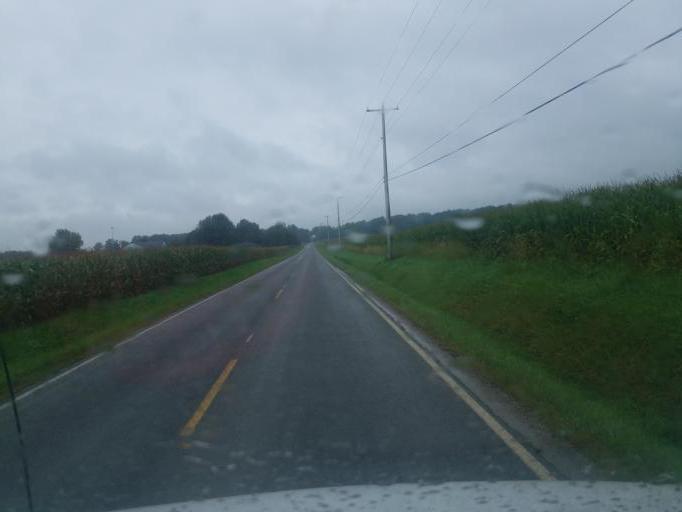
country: US
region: Ohio
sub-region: Wayne County
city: Rittman
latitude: 41.0110
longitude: -81.8151
